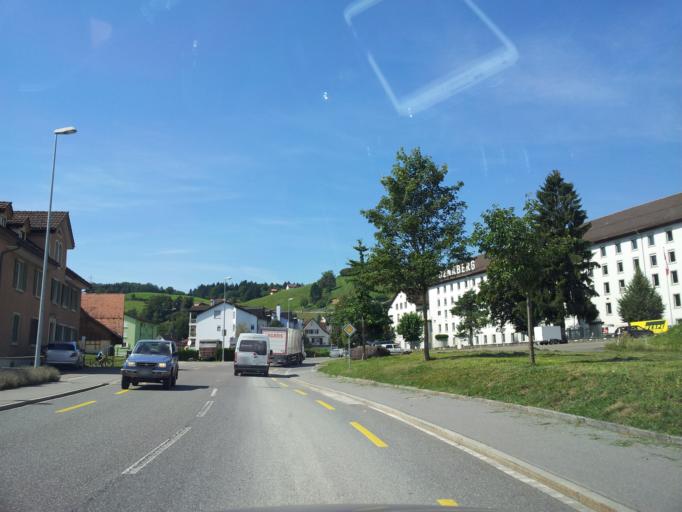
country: CH
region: Saint Gallen
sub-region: Wahlkreis See-Gaster
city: Uznach
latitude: 47.2295
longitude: 8.9658
